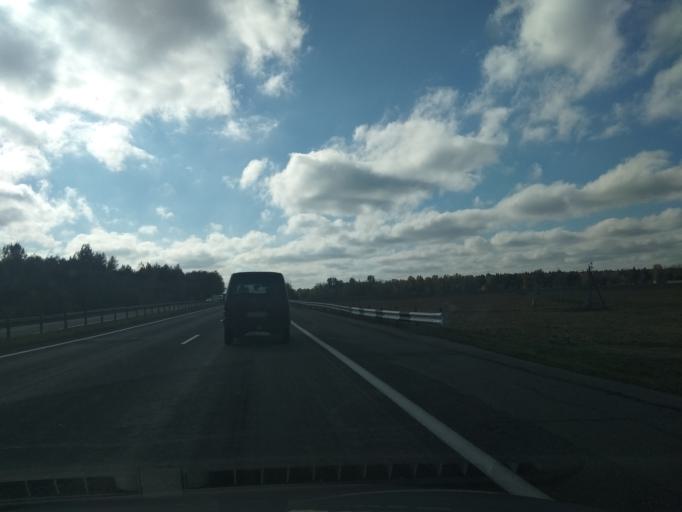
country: BY
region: Minsk
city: Enyerhyetykaw
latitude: 53.6025
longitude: 27.0450
